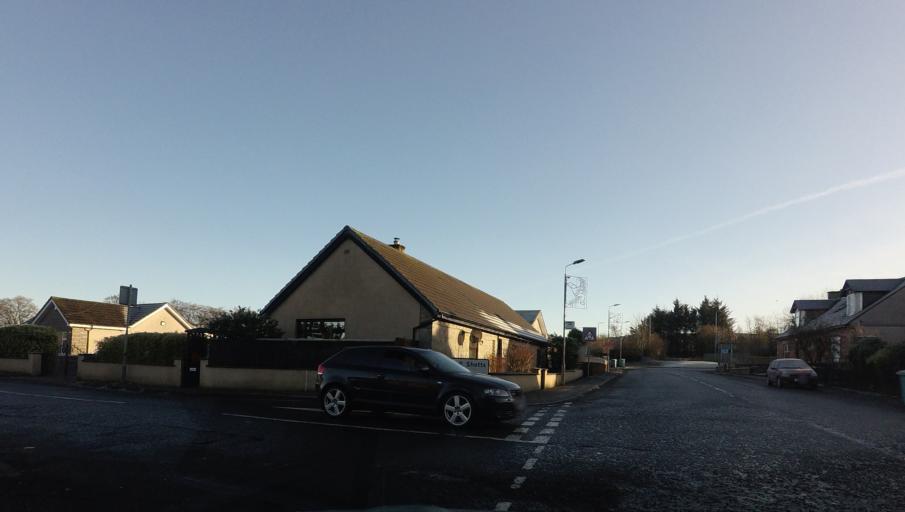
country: GB
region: Scotland
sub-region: North Lanarkshire
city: Shotts
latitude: 55.8007
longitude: -3.8409
